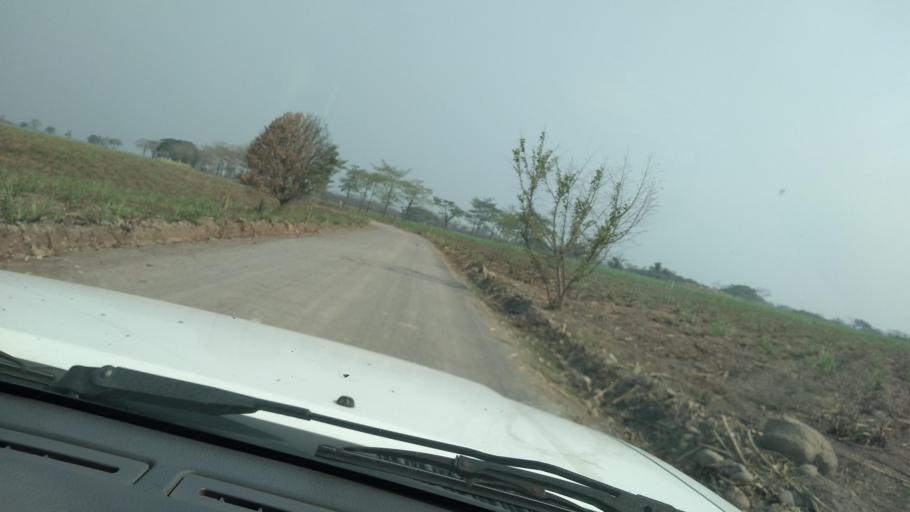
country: MX
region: Veracruz
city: Tezonapa
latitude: 18.6280
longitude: -96.6103
